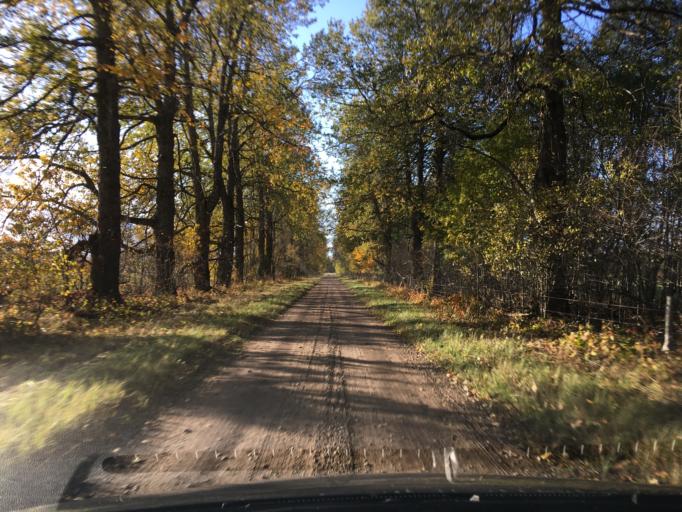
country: EE
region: Laeaene
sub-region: Lihula vald
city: Lihula
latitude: 58.5644
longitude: 23.7935
